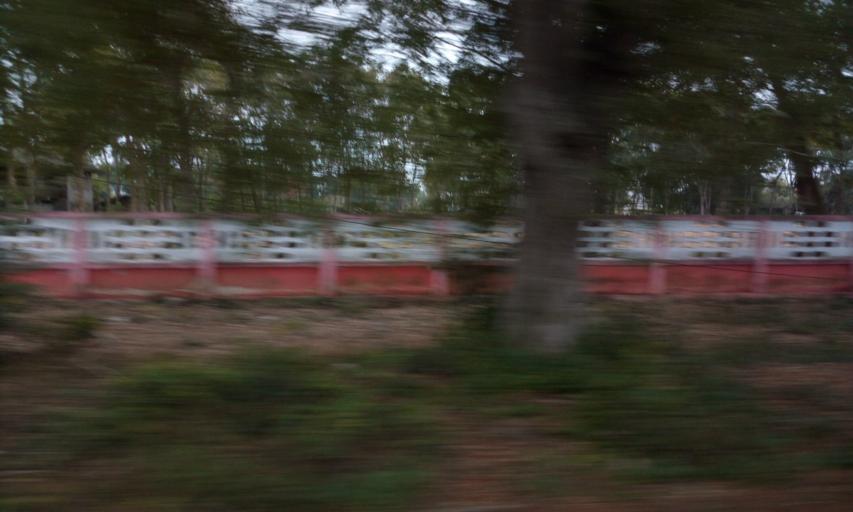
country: TH
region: Phayao
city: Chiang Kham
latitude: 19.5155
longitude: 100.3142
